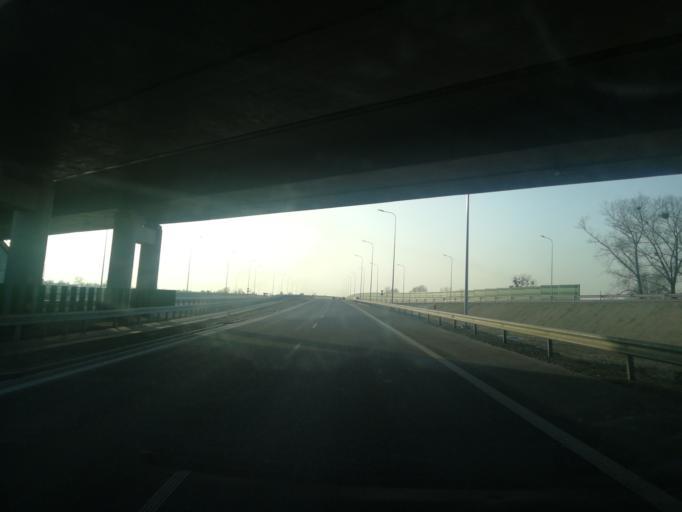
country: PL
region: Warmian-Masurian Voivodeship
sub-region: Powiat elblaski
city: Elblag
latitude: 54.1640
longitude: 19.3454
